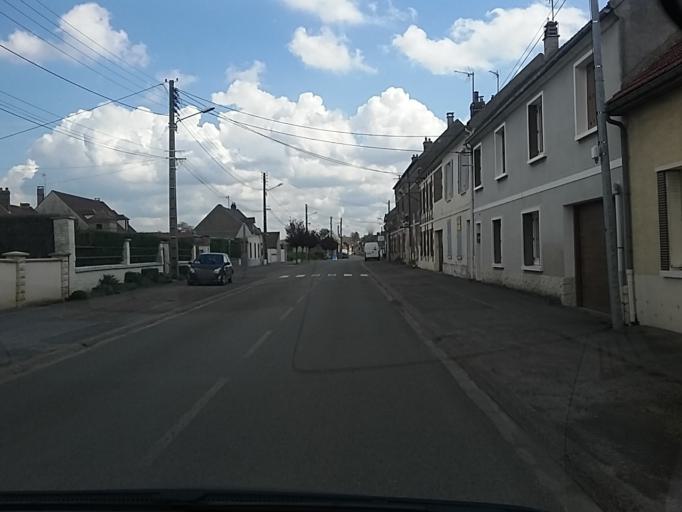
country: FR
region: Picardie
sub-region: Departement de l'Oise
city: Chevrieres
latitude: 49.3461
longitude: 2.6726
